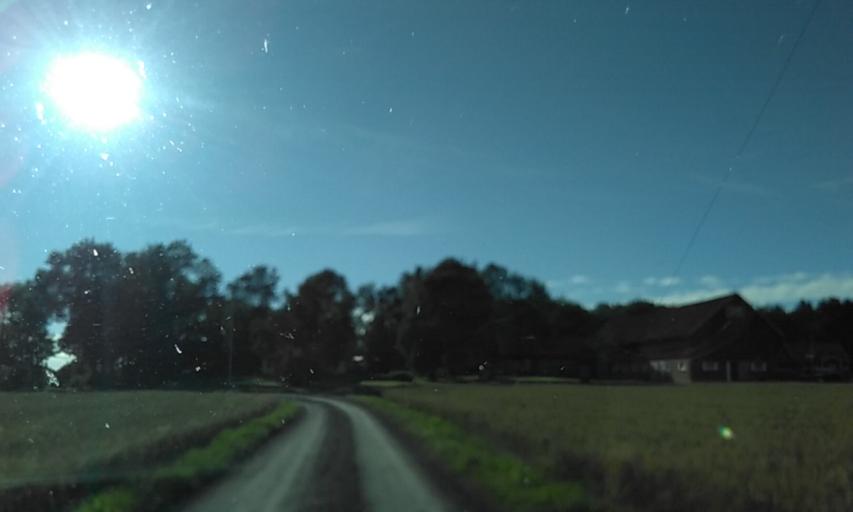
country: SE
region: Vaestra Goetaland
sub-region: Vara Kommun
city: Vara
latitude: 58.3702
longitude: 12.8423
